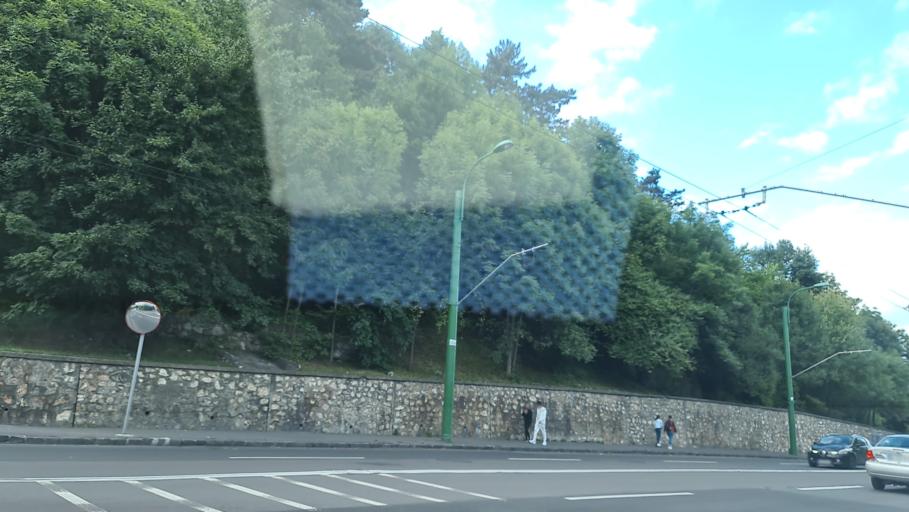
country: RO
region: Brasov
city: Brasov
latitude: 45.6457
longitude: 25.6189
